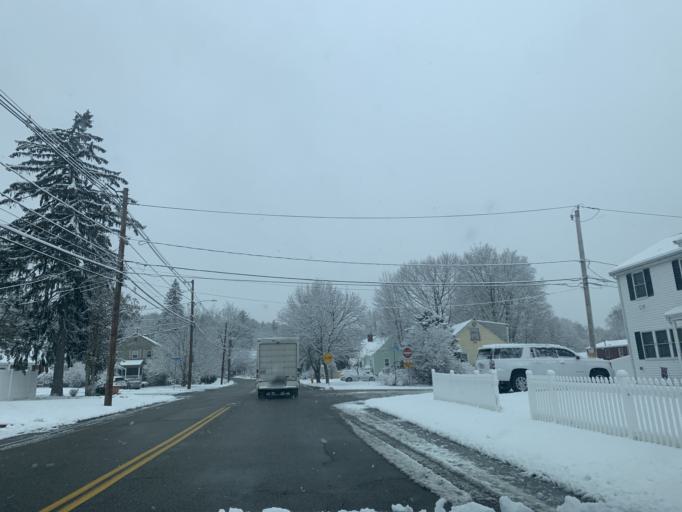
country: US
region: Massachusetts
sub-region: Norfolk County
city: Norwood
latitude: 42.2061
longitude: -71.1928
